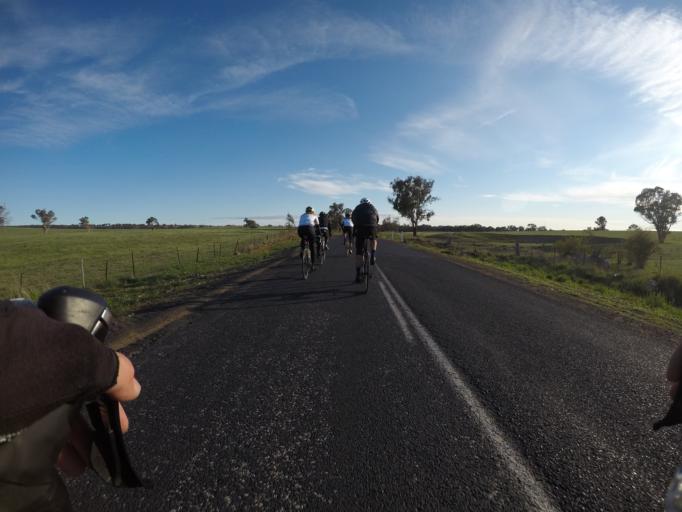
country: AU
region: New South Wales
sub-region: Cabonne
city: Molong
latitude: -32.9996
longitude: 148.7859
